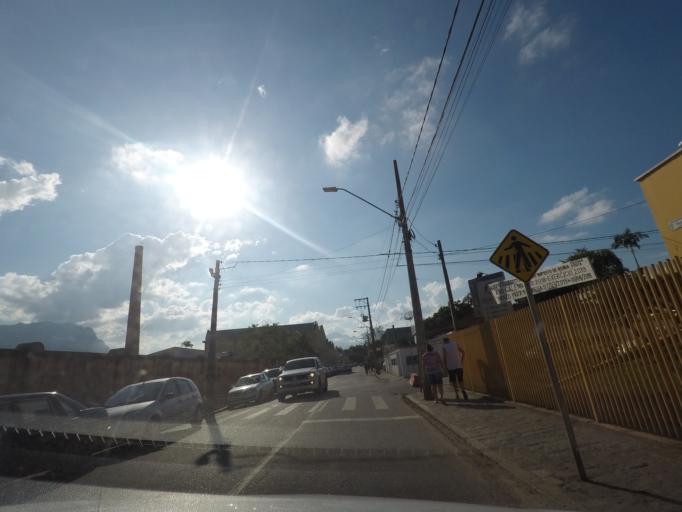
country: BR
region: Parana
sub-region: Antonina
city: Antonina
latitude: -25.4784
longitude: -48.8335
